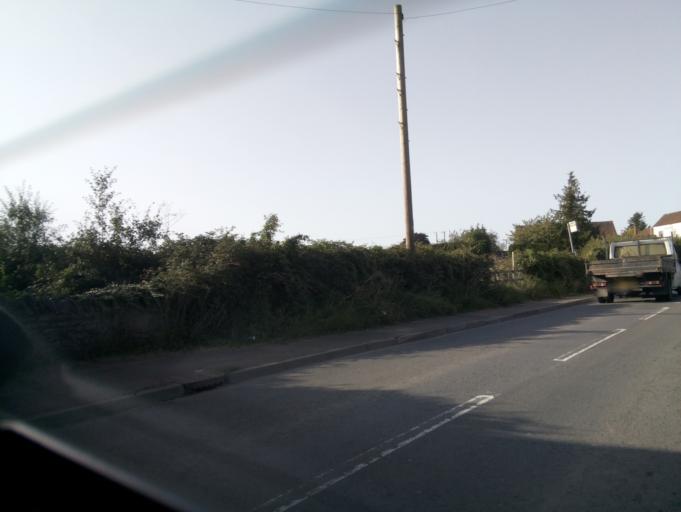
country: GB
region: England
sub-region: Gloucestershire
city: Newent
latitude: 51.9617
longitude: -2.3039
